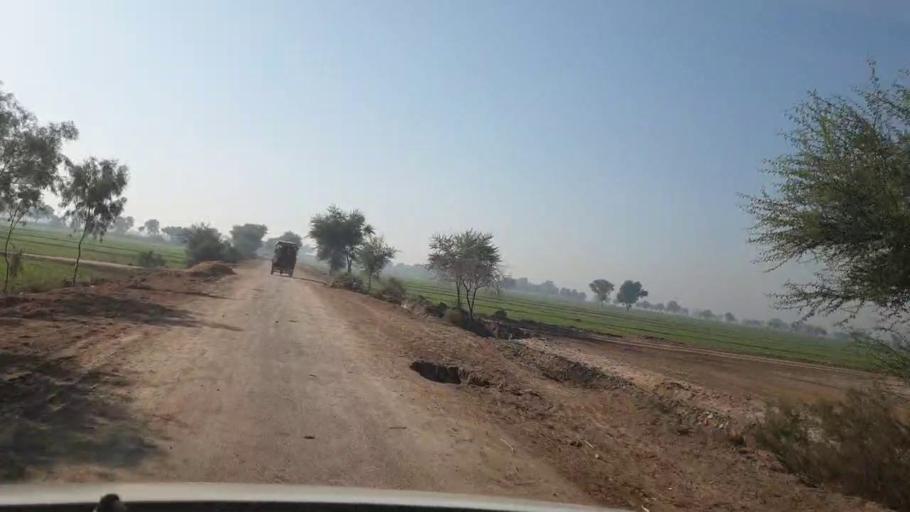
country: PK
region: Sindh
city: Dadu
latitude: 26.6460
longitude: 67.8218
